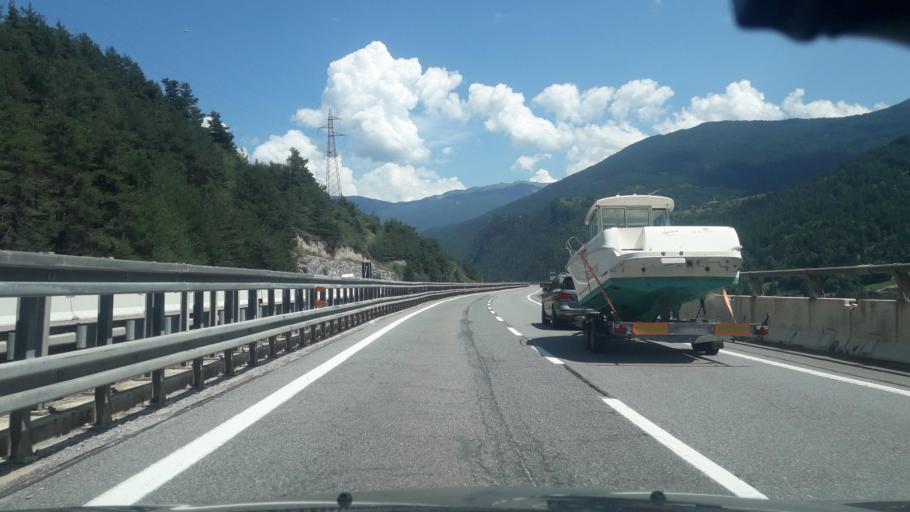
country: IT
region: Piedmont
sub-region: Provincia di Torino
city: Bardonecchia
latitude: 45.0511
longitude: 6.7497
